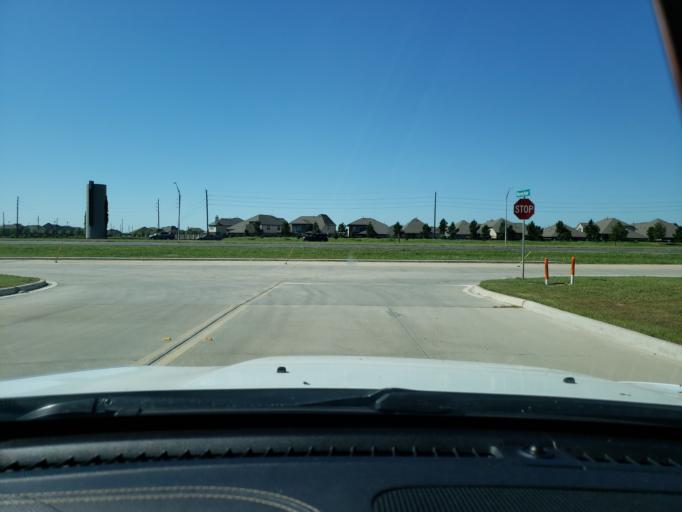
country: US
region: Texas
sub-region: Fort Bend County
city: Pecan Grove
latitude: 29.6608
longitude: -95.7221
